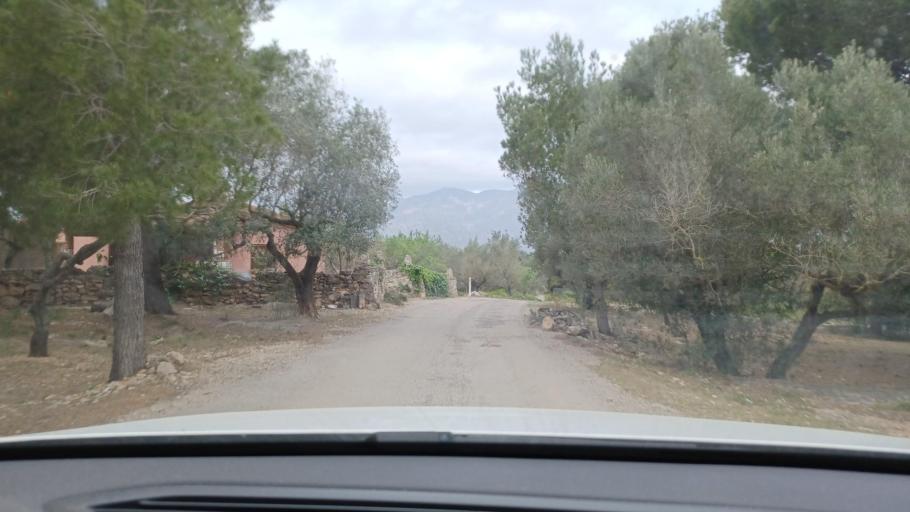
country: ES
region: Catalonia
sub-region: Provincia de Tarragona
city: Tortosa
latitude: 40.7914
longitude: 0.4750
